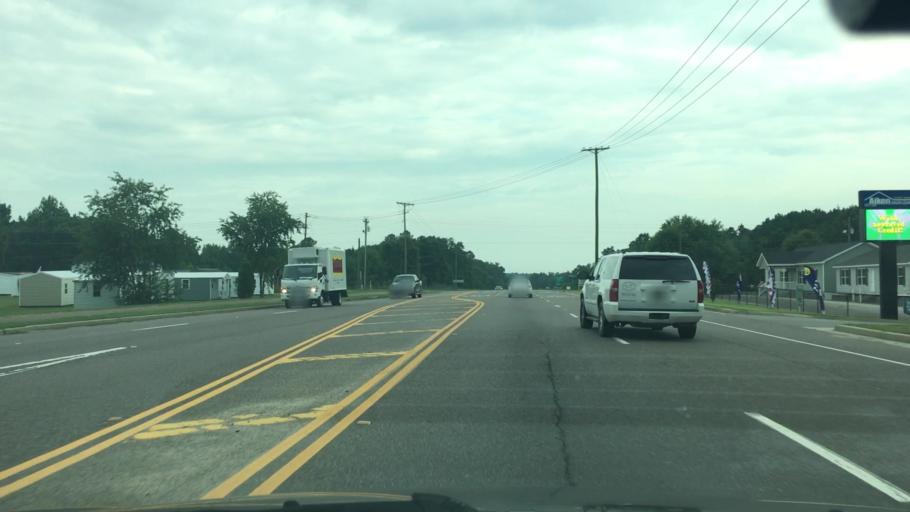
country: US
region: South Carolina
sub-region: Aiken County
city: Aiken
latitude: 33.5476
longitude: -81.6781
